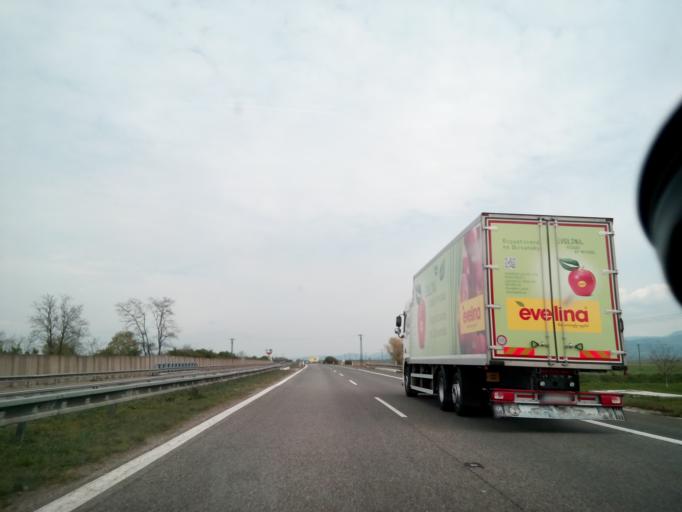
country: SK
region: Trnavsky
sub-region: Okres Trnava
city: Piestany
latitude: 48.6187
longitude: 17.8025
